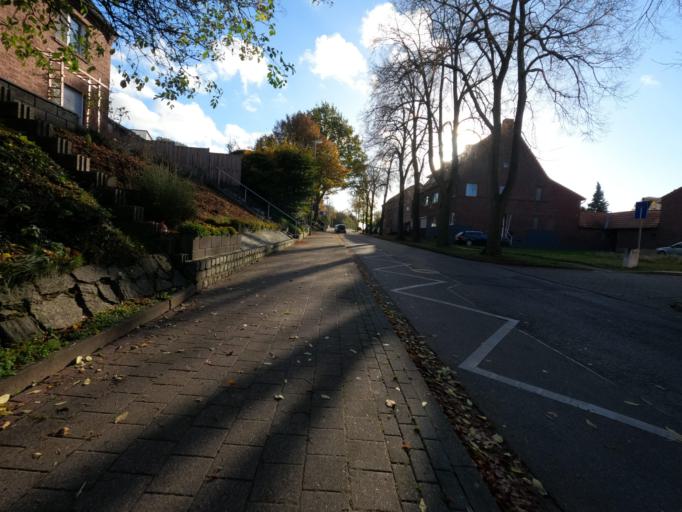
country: DE
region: North Rhine-Westphalia
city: Huckelhoven
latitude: 51.0543
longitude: 6.2313
